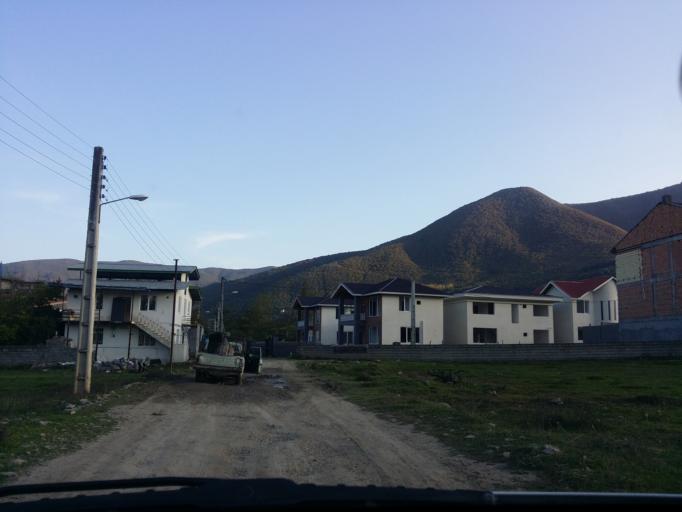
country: IR
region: Mazandaran
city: `Abbasabad
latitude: 36.5123
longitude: 51.1826
